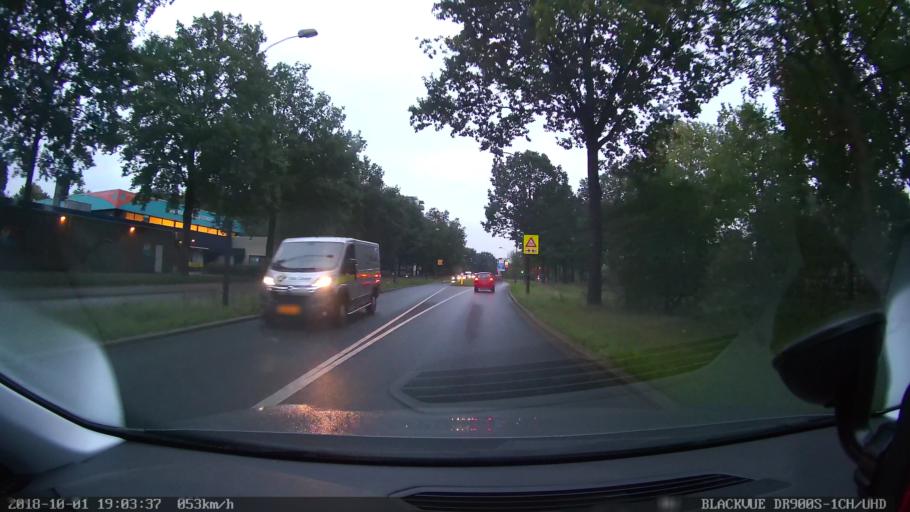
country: NL
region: Gelderland
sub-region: Gemeente Apeldoorn
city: Apeldoorn
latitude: 52.2276
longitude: 5.9931
